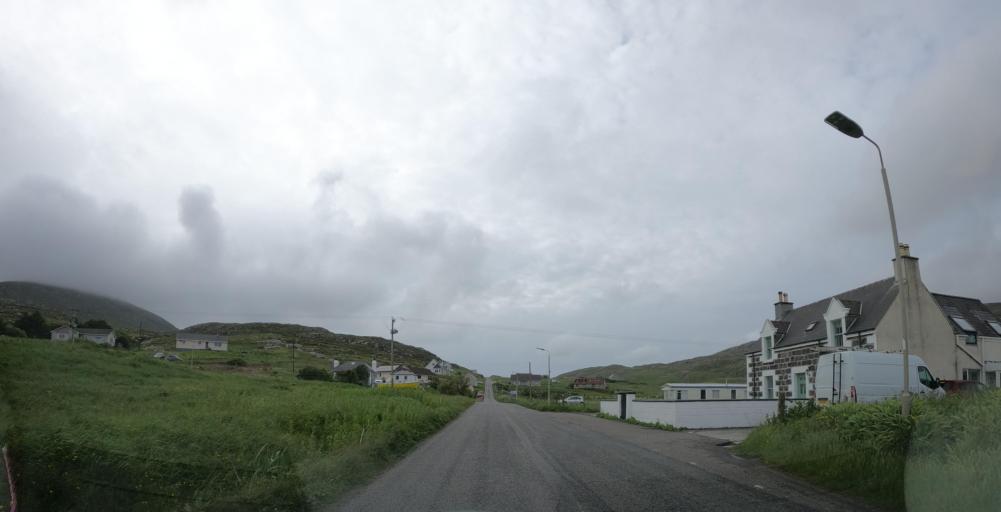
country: GB
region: Scotland
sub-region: Eilean Siar
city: Barra
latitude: 56.9585
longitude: -7.5042
